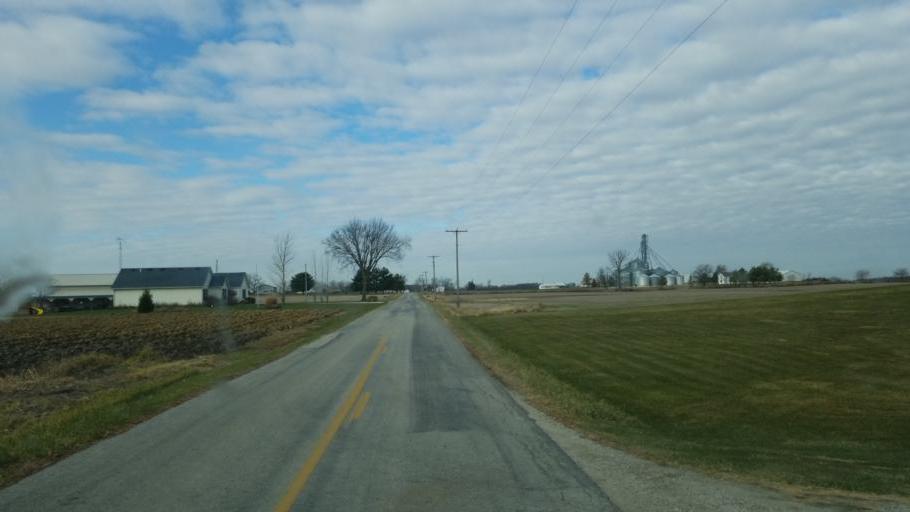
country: US
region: Ohio
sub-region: Union County
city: Richwood
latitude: 40.5145
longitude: -83.2697
